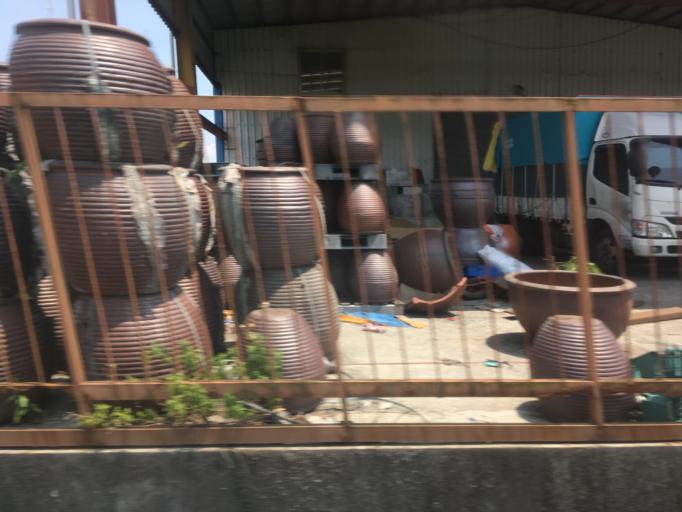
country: TW
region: Taiwan
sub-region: Yilan
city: Yilan
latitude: 24.6745
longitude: 121.8074
